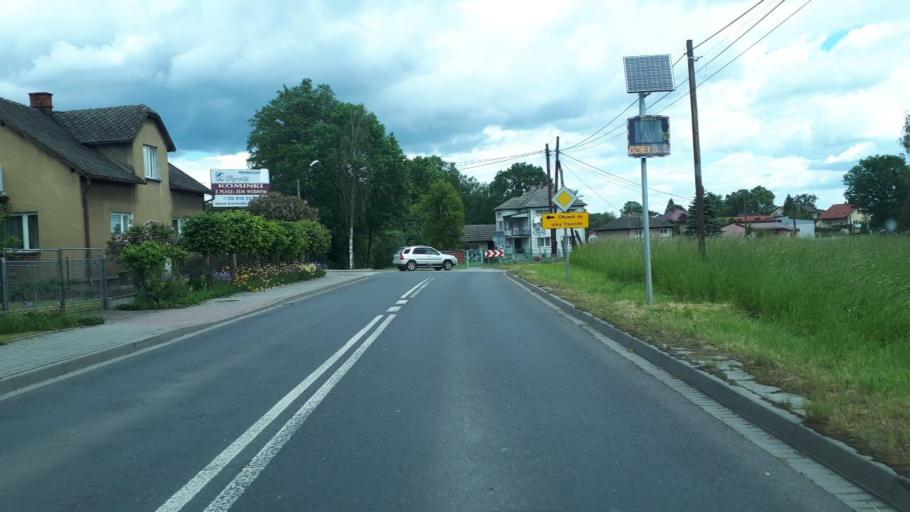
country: PL
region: Lesser Poland Voivodeship
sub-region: Powiat oswiecimski
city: Brzeszcze
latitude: 49.9575
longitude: 19.1373
